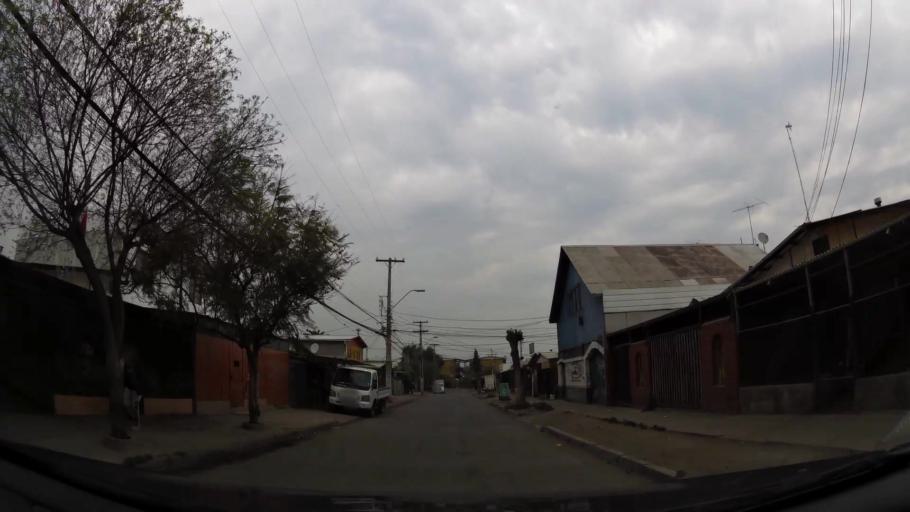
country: CL
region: Santiago Metropolitan
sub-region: Provincia de Chacabuco
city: Chicureo Abajo
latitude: -33.1910
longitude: -70.6647
